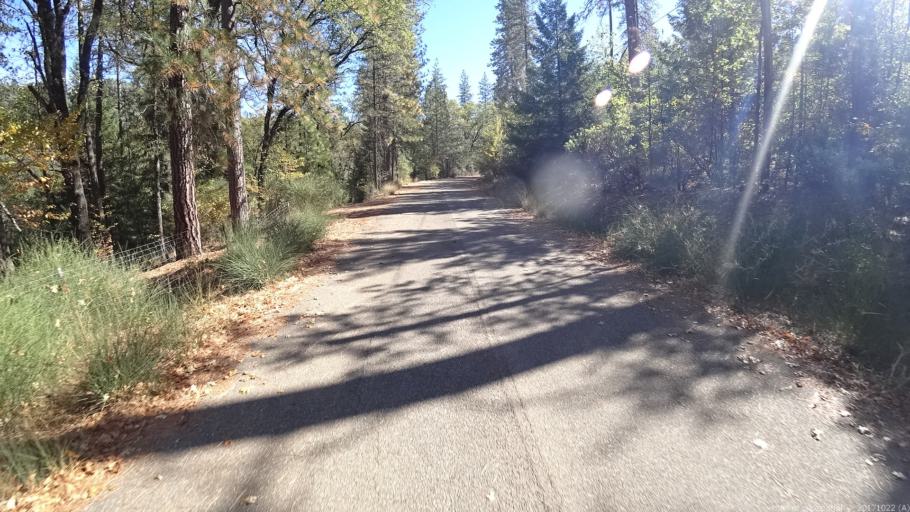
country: US
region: California
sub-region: Shasta County
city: Central Valley (historical)
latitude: 40.9425
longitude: -122.4255
